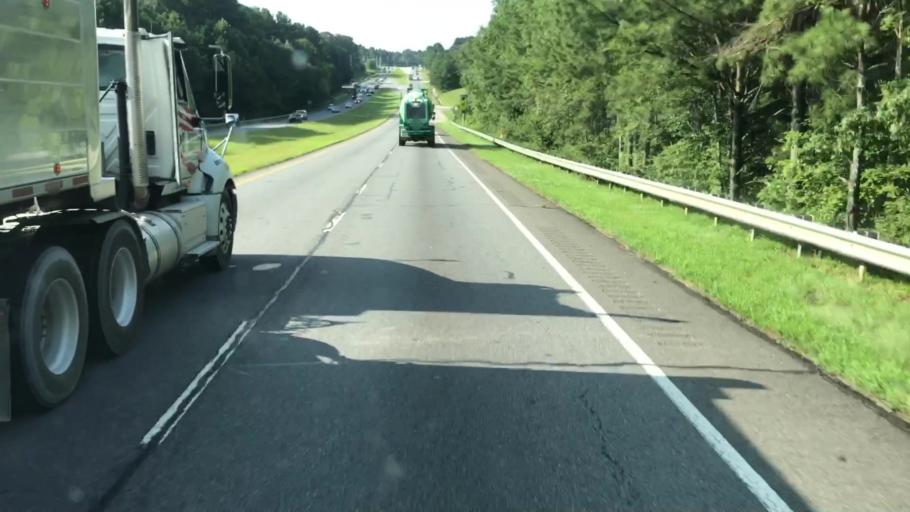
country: US
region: Georgia
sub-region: Gwinnett County
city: Lawrenceville
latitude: 34.0280
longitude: -83.9865
